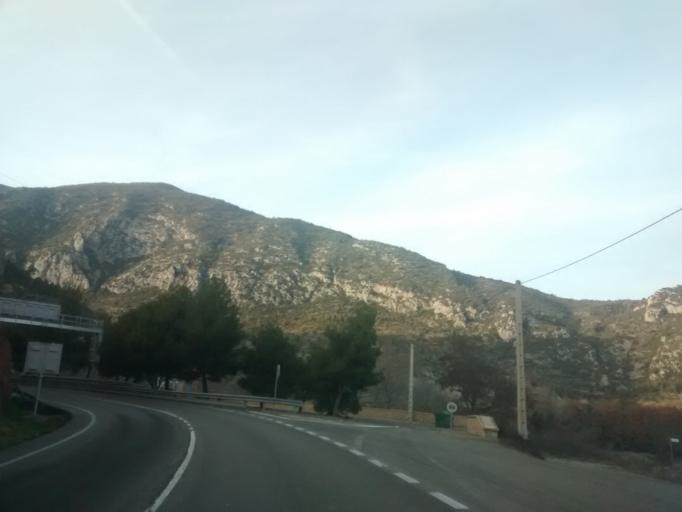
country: ES
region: Catalonia
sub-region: Provincia de Lleida
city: Coll de Nargo
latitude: 42.1748
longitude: 1.3203
